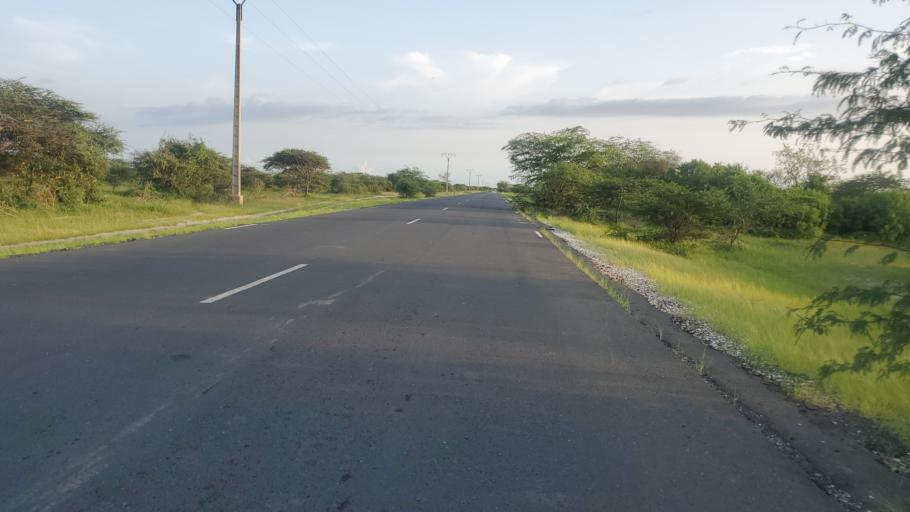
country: SN
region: Saint-Louis
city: Saint-Louis
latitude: 16.1830
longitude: -16.4095
